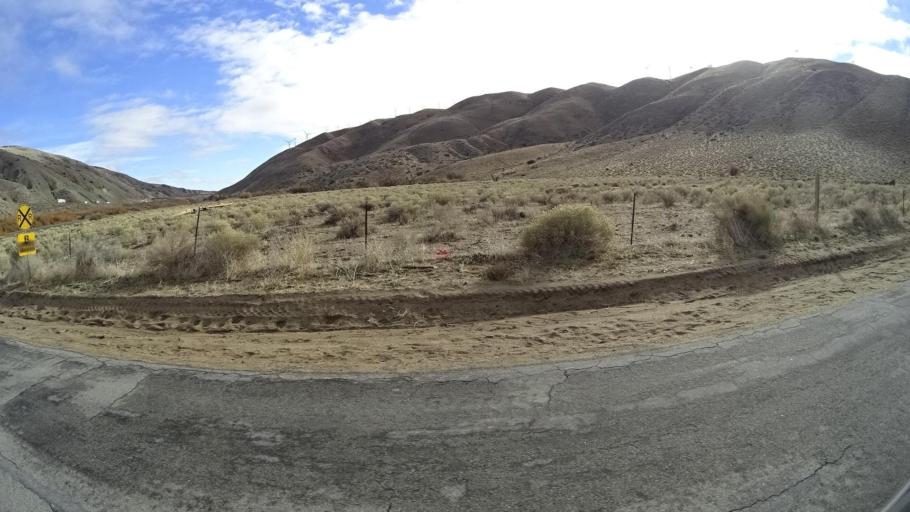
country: US
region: California
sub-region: Kern County
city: Mojave
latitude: 35.0945
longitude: -118.3068
